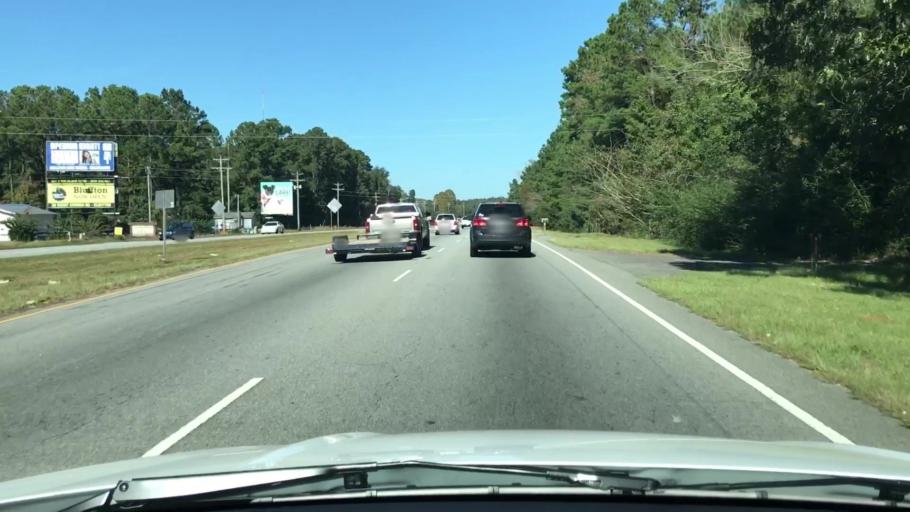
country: US
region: South Carolina
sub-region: Beaufort County
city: Bluffton
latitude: 32.3149
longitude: -80.9344
